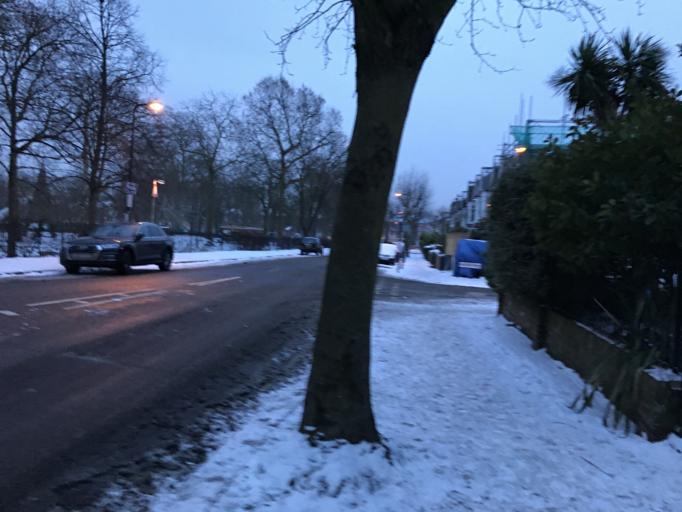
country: GB
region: England
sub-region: Greater London
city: Bayswater
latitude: 51.5351
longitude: -0.2128
